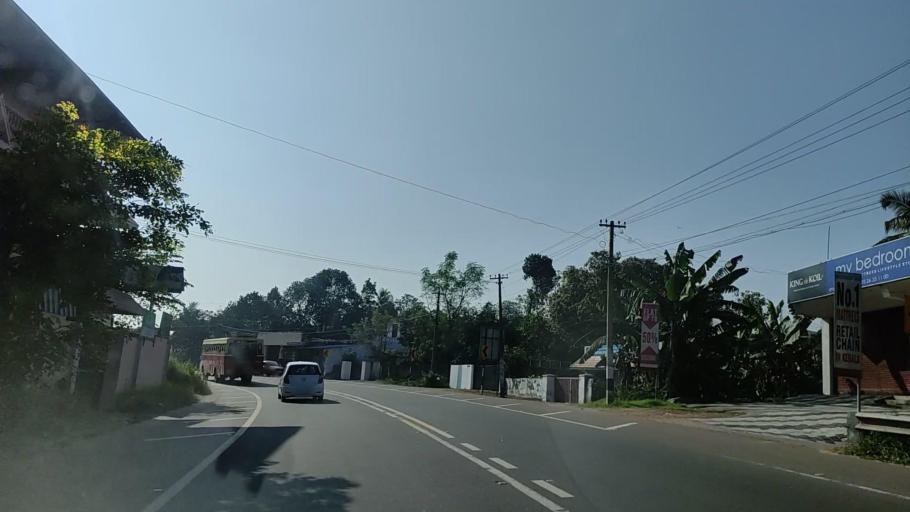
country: IN
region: Kerala
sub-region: Kollam
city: Punalur
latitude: 8.9018
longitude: 76.8563
